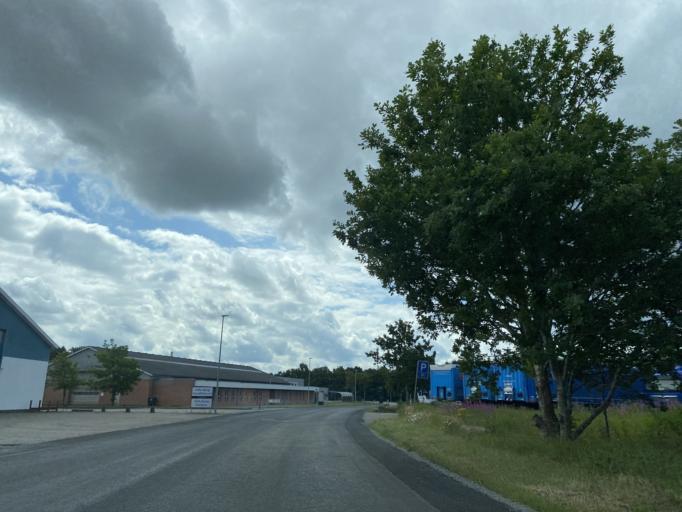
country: DK
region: Central Jutland
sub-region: Silkeborg Kommune
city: Silkeborg
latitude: 56.2028
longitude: 9.5790
